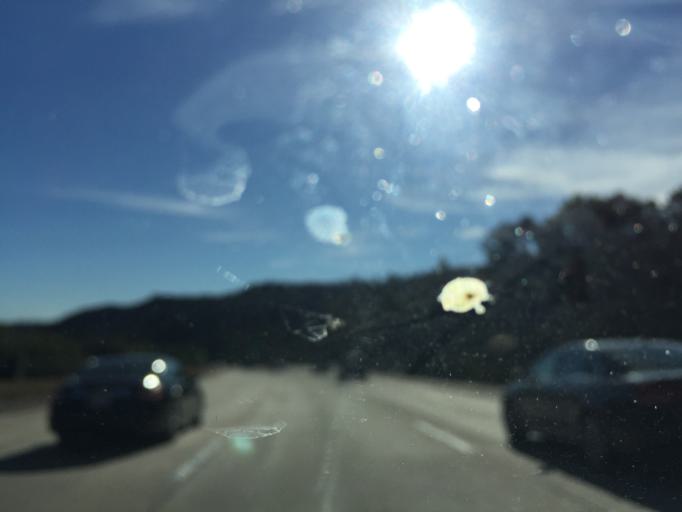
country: US
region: California
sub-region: San Diego County
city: La Jolla
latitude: 32.8490
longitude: -117.2356
